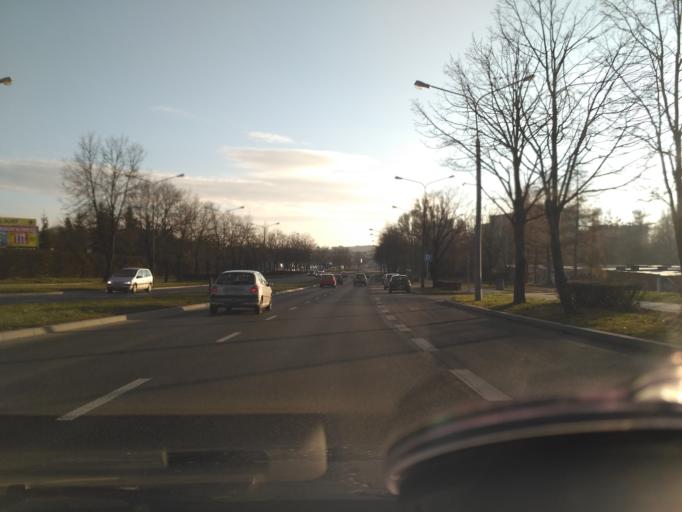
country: PL
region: Lublin Voivodeship
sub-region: Powiat lubelski
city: Lublin
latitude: 51.2633
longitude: 22.5668
